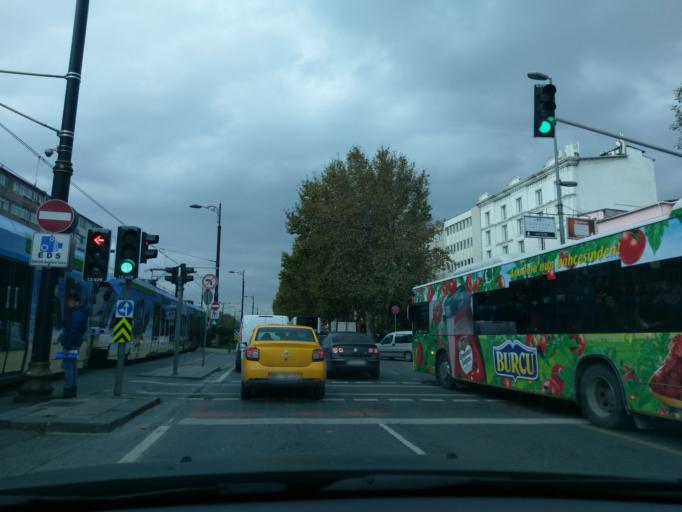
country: TR
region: Istanbul
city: Istanbul
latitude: 41.0164
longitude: 28.9312
